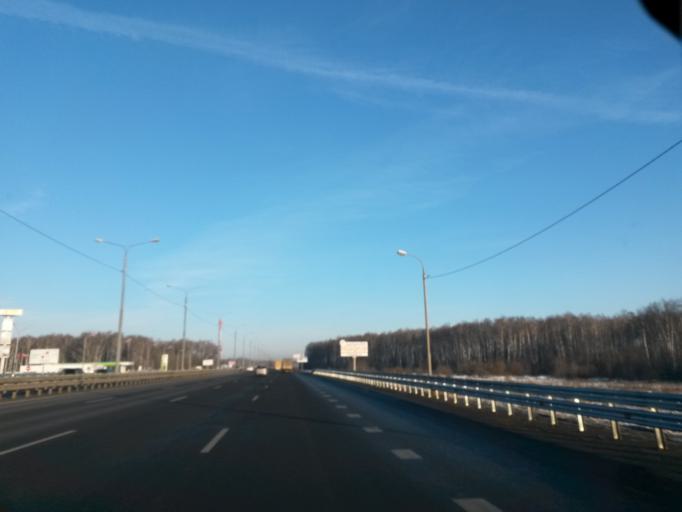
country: RU
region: Moskovskaya
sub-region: Podol'skiy Rayon
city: Podol'sk
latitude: 55.3911
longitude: 37.6052
